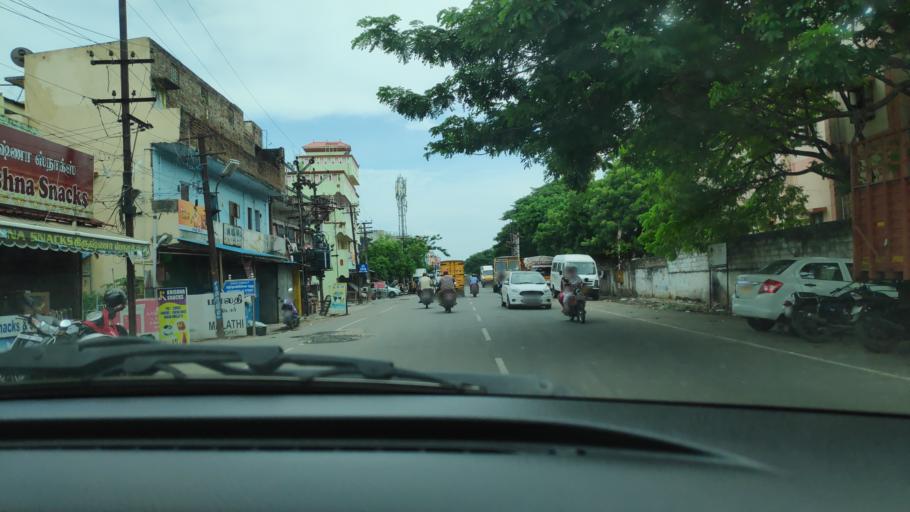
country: IN
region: Tamil Nadu
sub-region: Kancheepuram
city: Pallavaram
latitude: 12.9302
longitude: 80.1274
